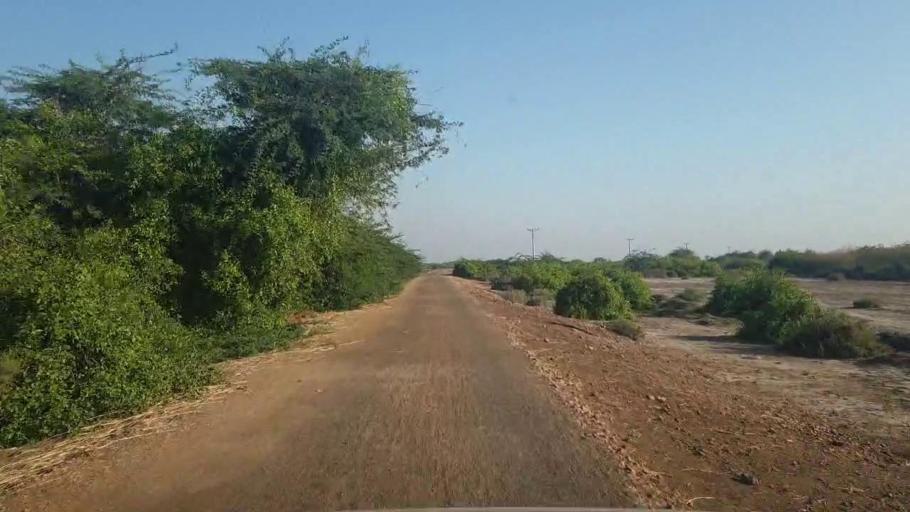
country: PK
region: Sindh
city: Badin
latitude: 24.7329
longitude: 68.8685
